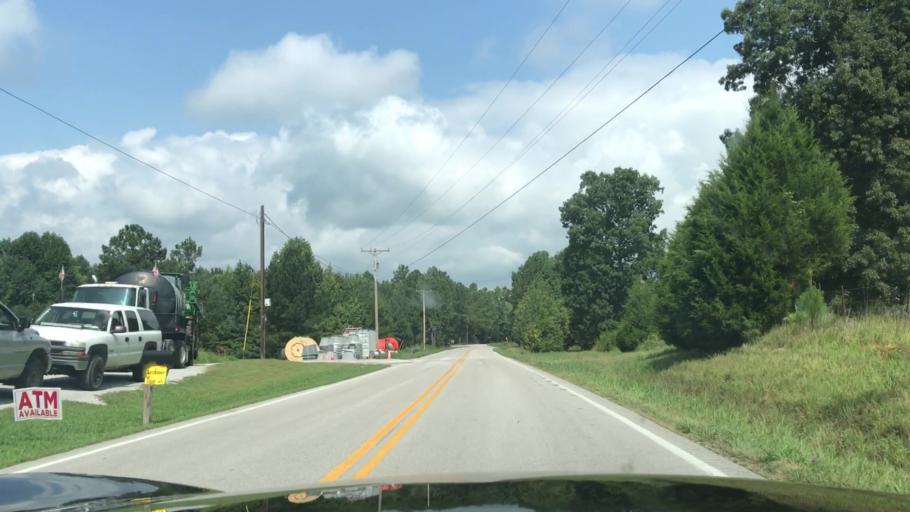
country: US
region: Kentucky
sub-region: Ohio County
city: Oak Grove
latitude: 37.1903
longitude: -86.8806
